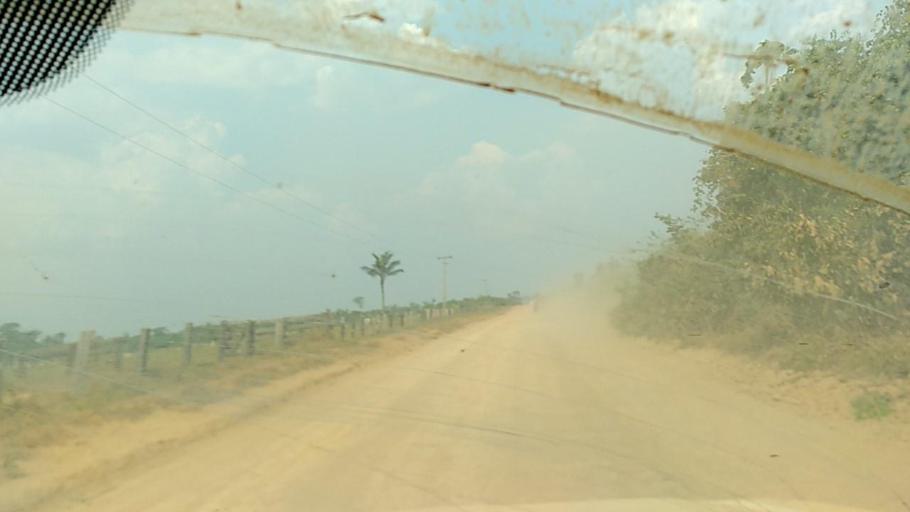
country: BR
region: Rondonia
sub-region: Porto Velho
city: Porto Velho
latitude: -8.6833
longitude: -63.2142
